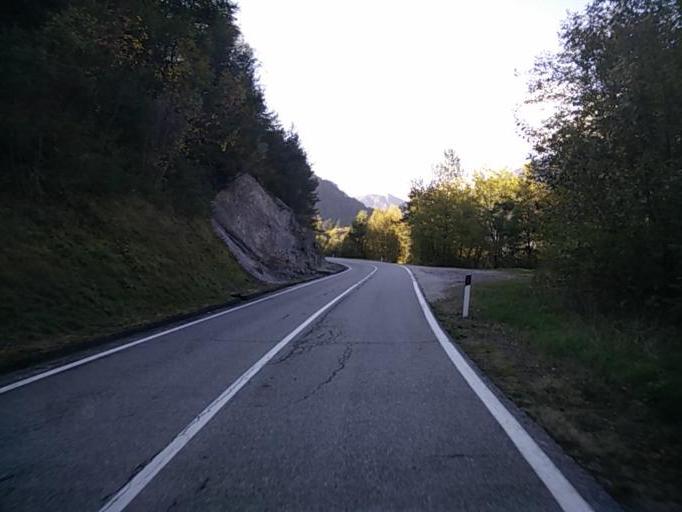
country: IT
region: Lombardy
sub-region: Provincia di Brescia
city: Anfo
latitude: 45.7485
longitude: 10.5058
